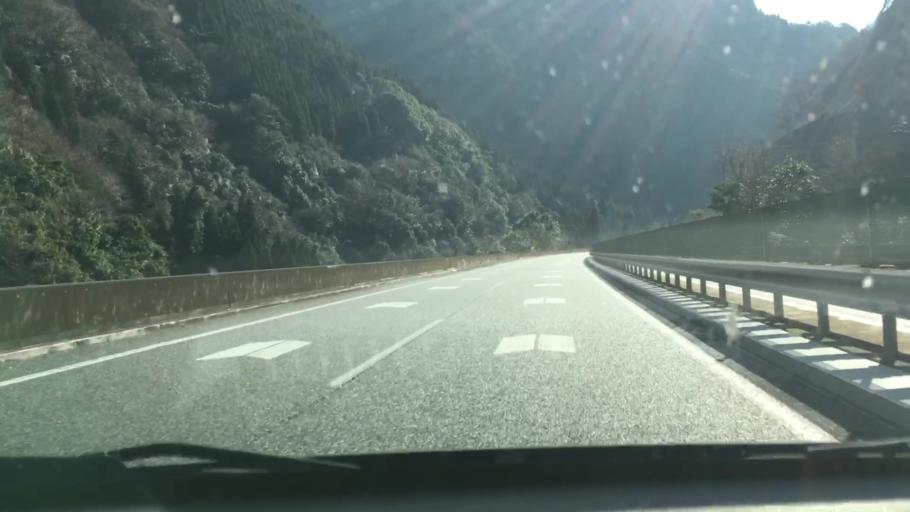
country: JP
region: Kumamoto
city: Hitoyoshi
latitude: 32.3219
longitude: 130.7578
